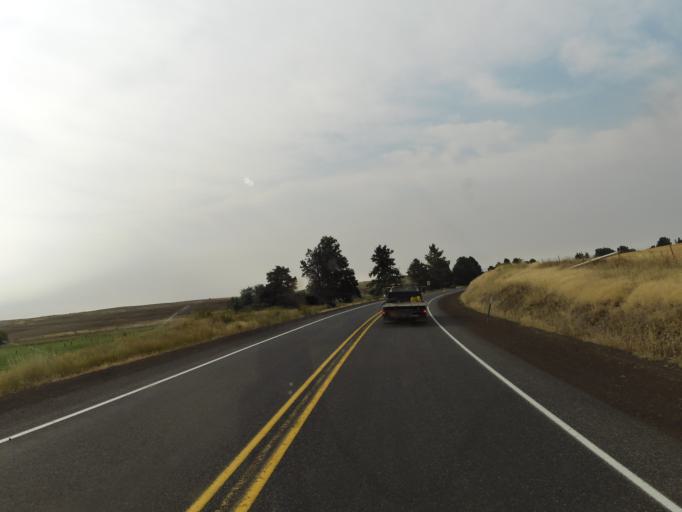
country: US
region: Oregon
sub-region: Sherman County
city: Moro
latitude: 45.3717
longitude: -120.7820
